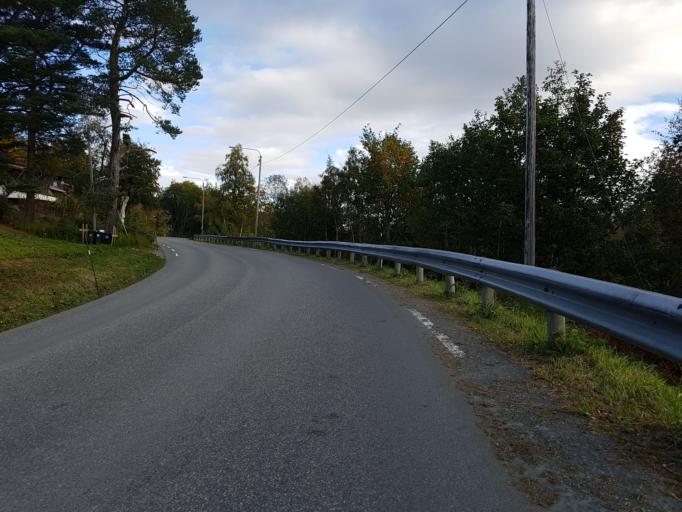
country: NO
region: Sor-Trondelag
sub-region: Klaebu
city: Klaebu
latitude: 63.3951
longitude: 10.5265
